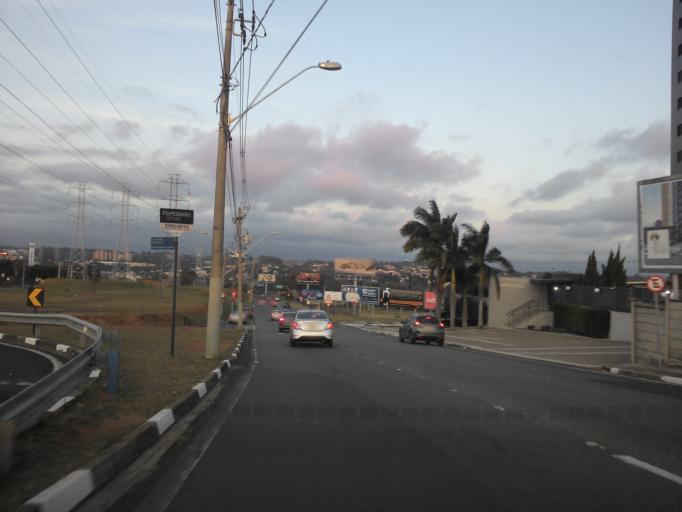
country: BR
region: Sao Paulo
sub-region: Campinas
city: Campinas
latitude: -22.8941
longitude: -47.0280
